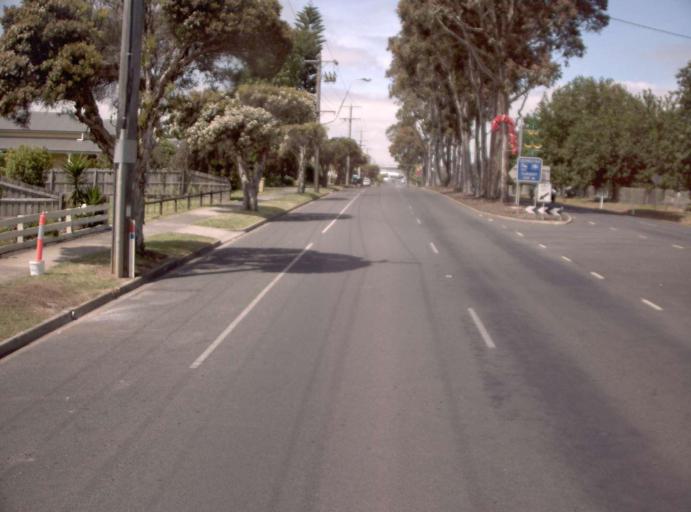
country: AU
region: Victoria
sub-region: Baw Baw
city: Warragul
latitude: -38.4688
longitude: 145.9501
